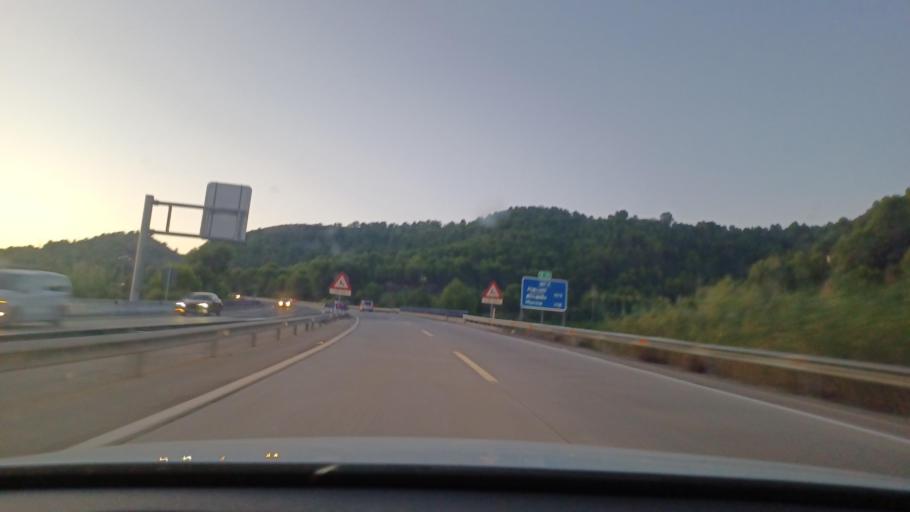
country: ES
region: Valencia
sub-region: Provincia de Valencia
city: L'Alqueria de la Comtessa
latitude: 38.9210
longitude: -0.1378
